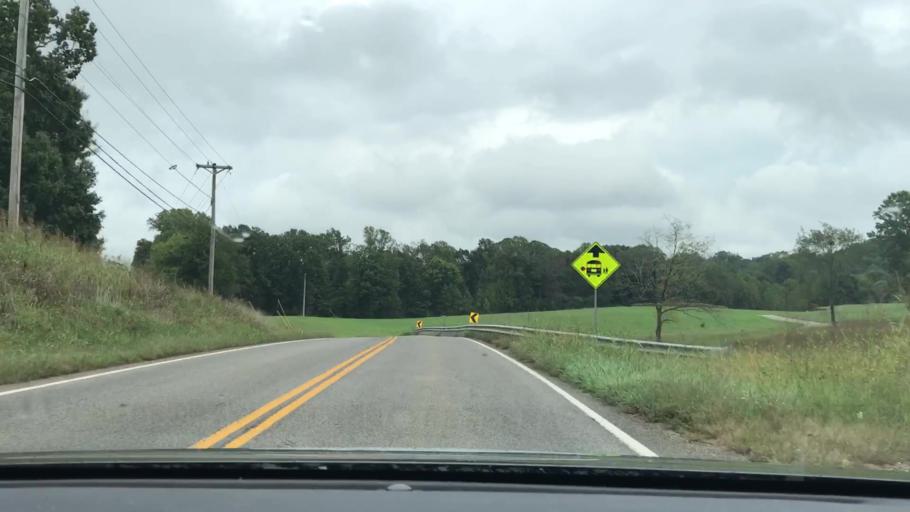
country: US
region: Kentucky
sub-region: Monroe County
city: Tompkinsville
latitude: 36.6364
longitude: -85.7681
